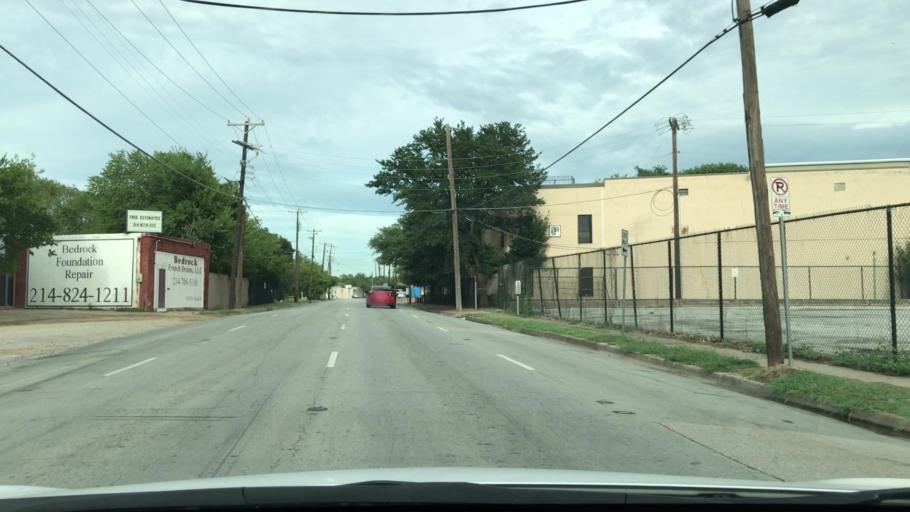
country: US
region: Texas
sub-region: Dallas County
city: Dallas
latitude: 32.7838
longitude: -96.7626
